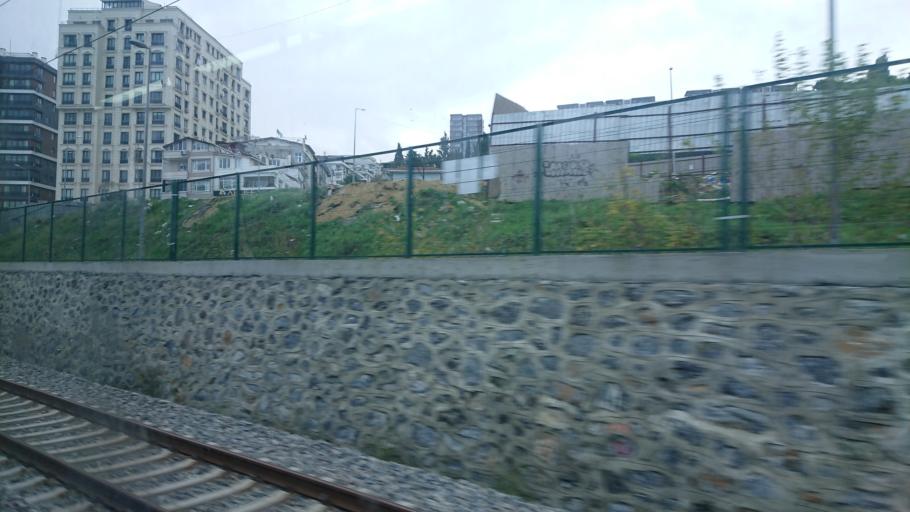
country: TR
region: Istanbul
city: Mahmutbey
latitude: 41.0039
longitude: 28.7721
